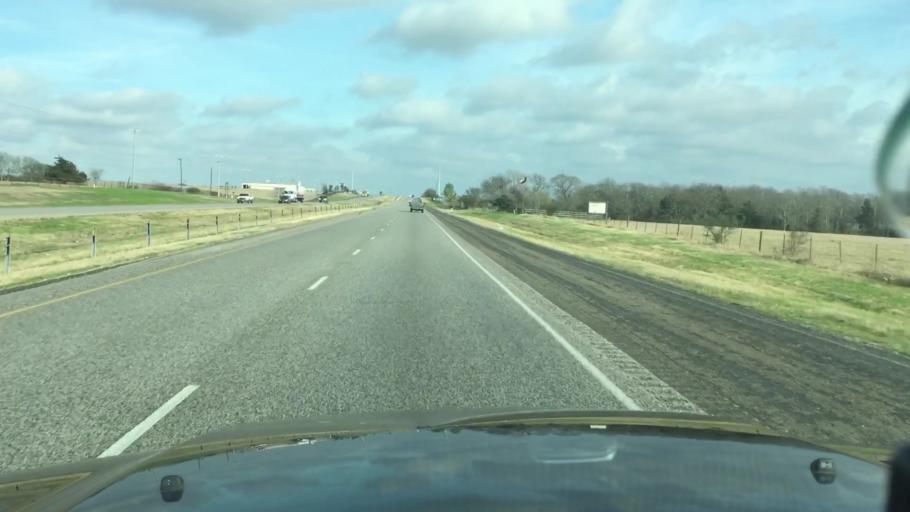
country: US
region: Texas
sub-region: Washington County
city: Brenham
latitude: 30.1364
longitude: -96.3350
